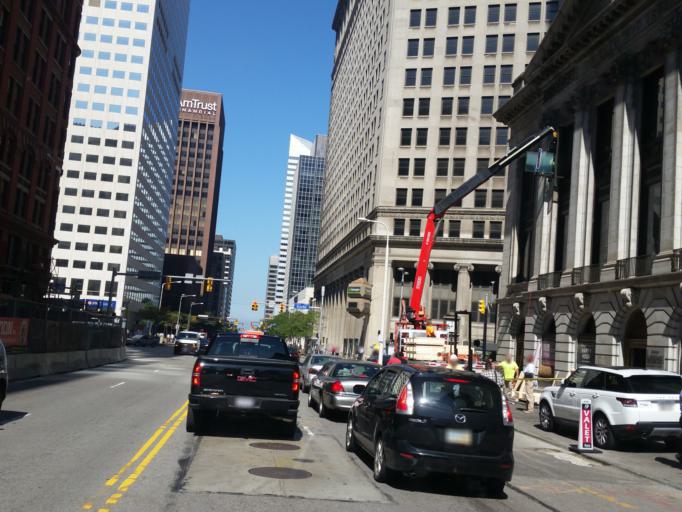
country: US
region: Ohio
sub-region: Cuyahoga County
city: Cleveland
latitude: 41.4997
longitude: -81.6862
